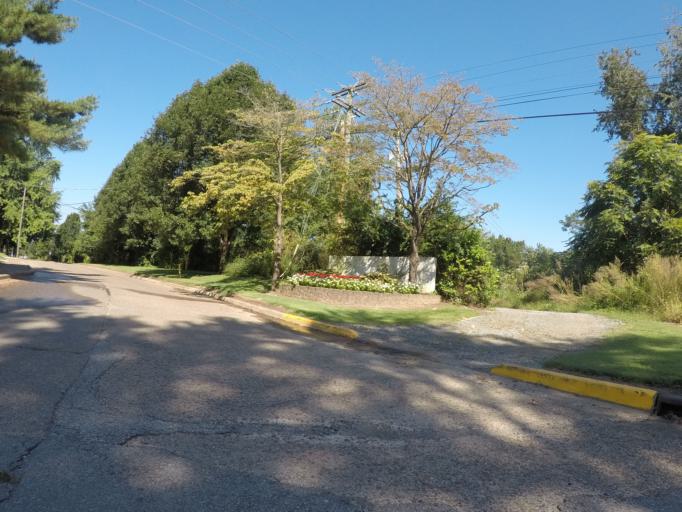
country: US
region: West Virginia
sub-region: Wayne County
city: Ceredo
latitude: 38.3992
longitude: -82.5641
